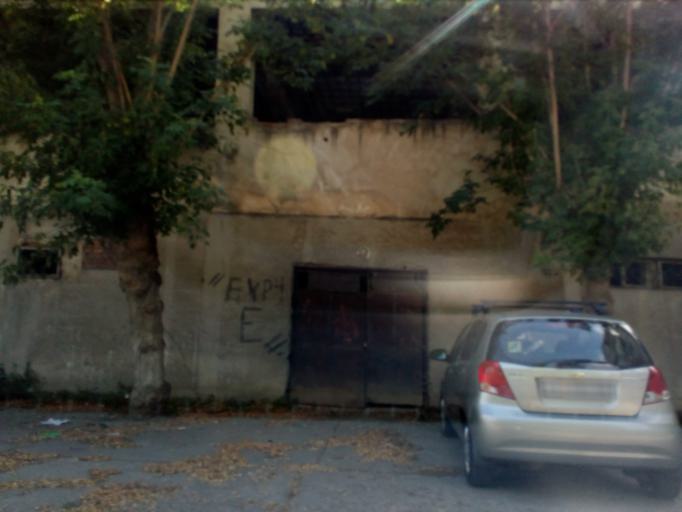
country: MK
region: Veles
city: Veles
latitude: 41.7194
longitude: 21.7857
